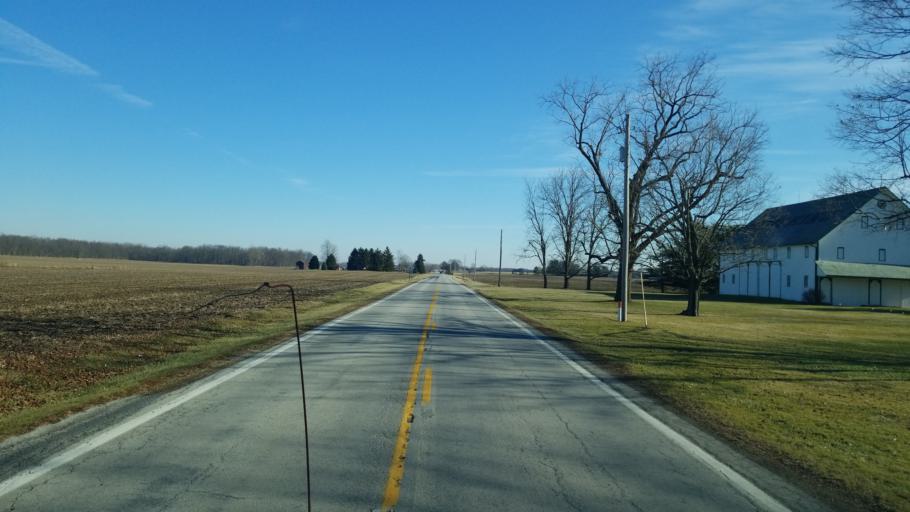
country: US
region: Ohio
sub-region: Henry County
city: Liberty Center
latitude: 41.4152
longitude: -83.9697
